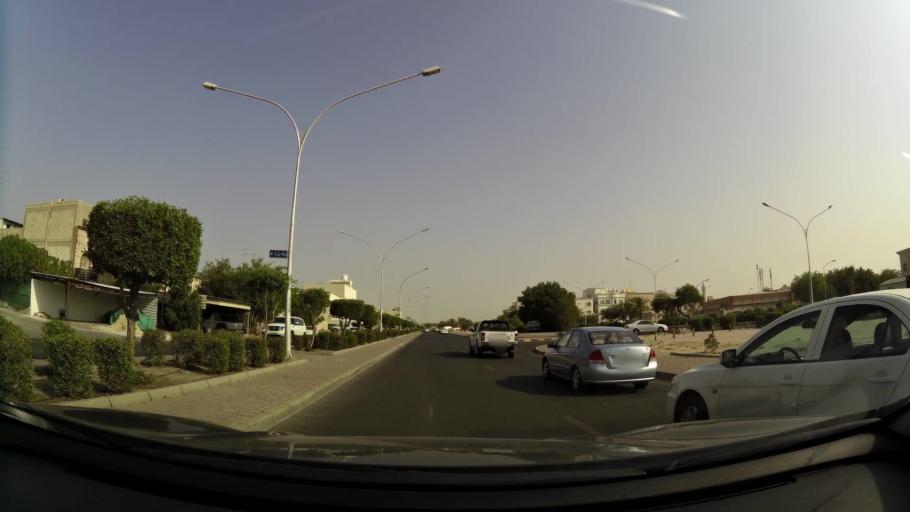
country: KW
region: Muhafazat al Jahra'
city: Al Jahra'
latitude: 29.3340
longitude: 47.7012
